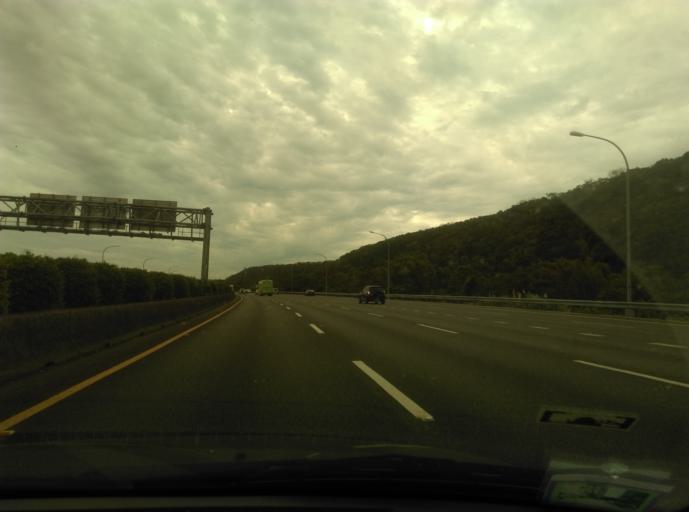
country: TW
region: Taiwan
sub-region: Taoyuan
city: Taoyuan
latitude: 24.9375
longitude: 121.3199
